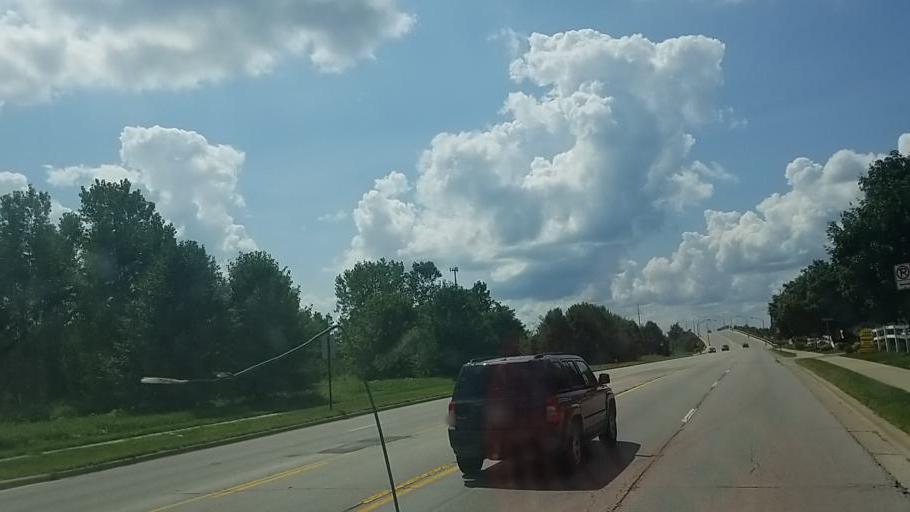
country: US
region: Ohio
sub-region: Franklin County
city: Worthington
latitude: 40.1191
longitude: -82.9984
